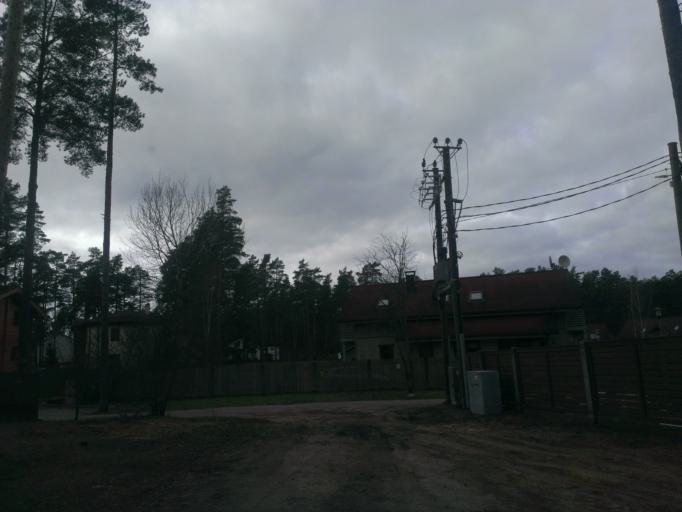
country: LV
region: Riga
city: Bergi
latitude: 57.0049
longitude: 24.3328
